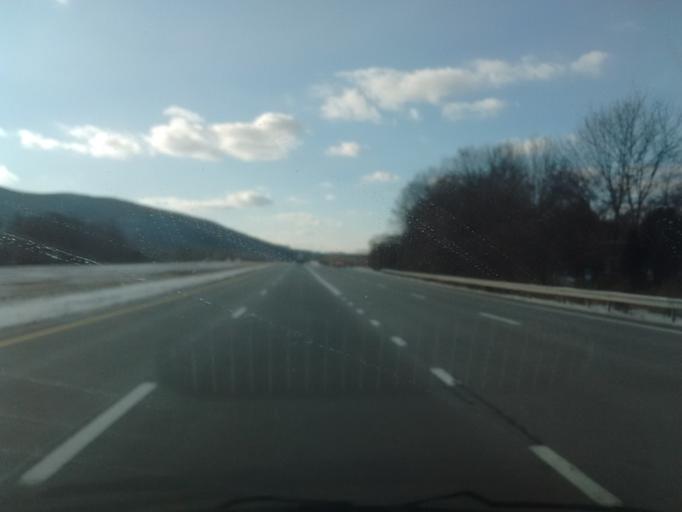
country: US
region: New York
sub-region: Dutchess County
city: Fishkill
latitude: 41.5247
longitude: -73.8857
